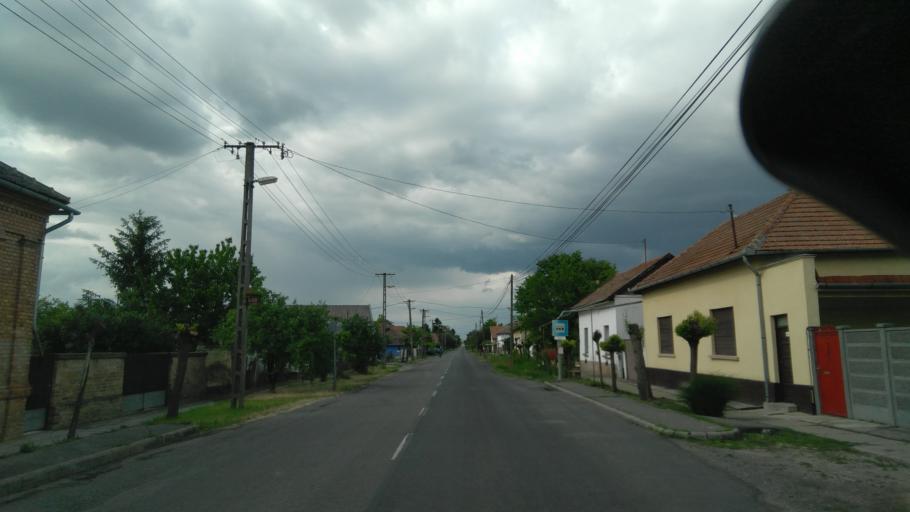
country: HU
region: Bekes
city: Gadoros
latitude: 46.6579
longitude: 20.5900
